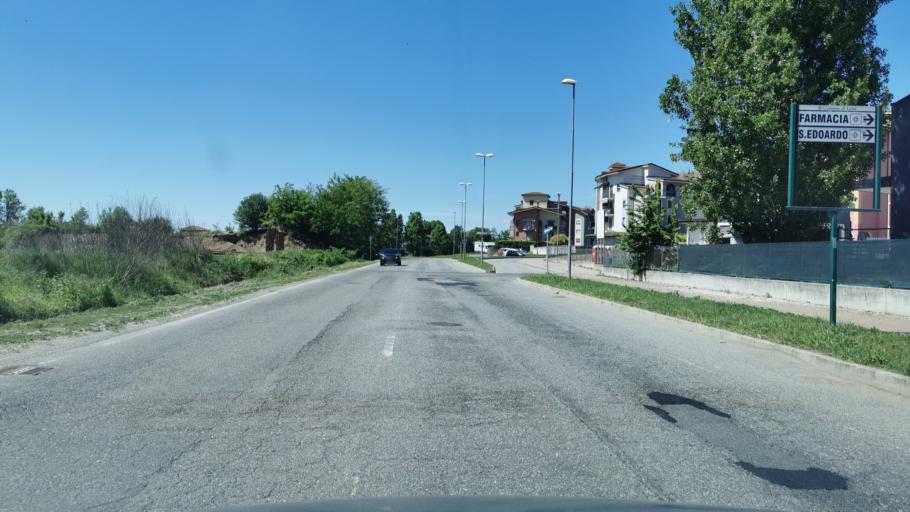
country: IT
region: Piedmont
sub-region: Provincia di Torino
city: Leini
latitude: 45.1803
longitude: 7.7206
